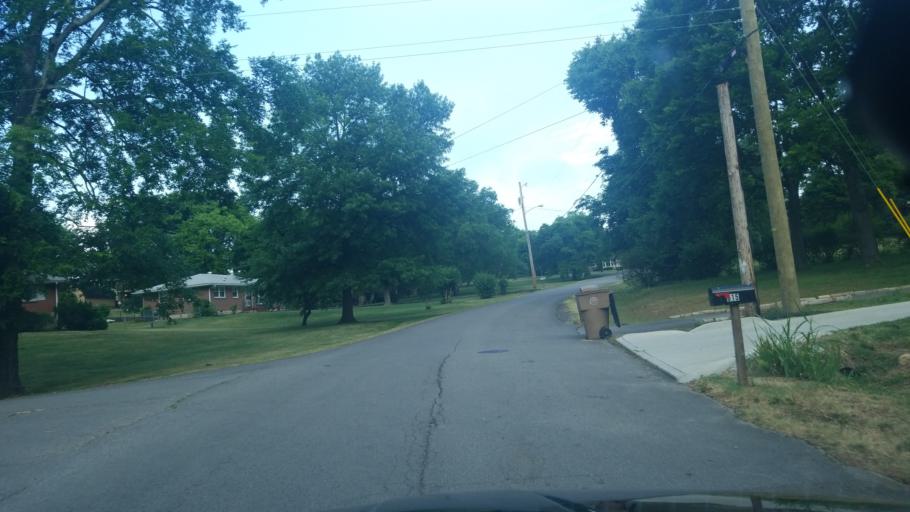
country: US
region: Tennessee
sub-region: Davidson County
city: Nashville
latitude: 36.2349
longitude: -86.7417
